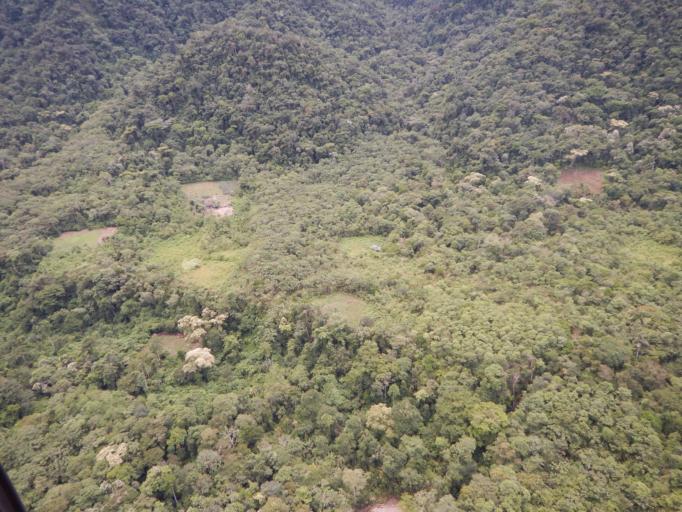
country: BO
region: Cochabamba
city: Totora
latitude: -17.4498
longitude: -65.0104
